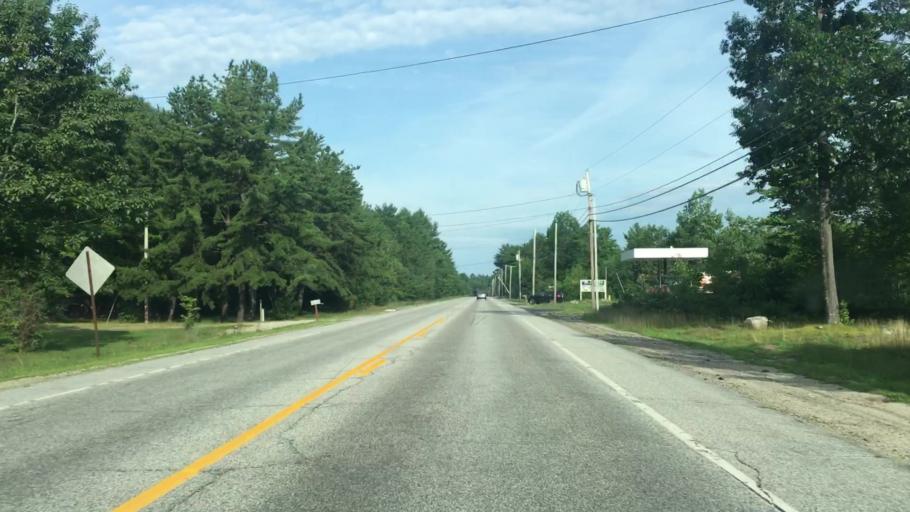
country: US
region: Maine
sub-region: Cumberland County
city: Steep Falls
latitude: 43.7337
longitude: -70.6174
